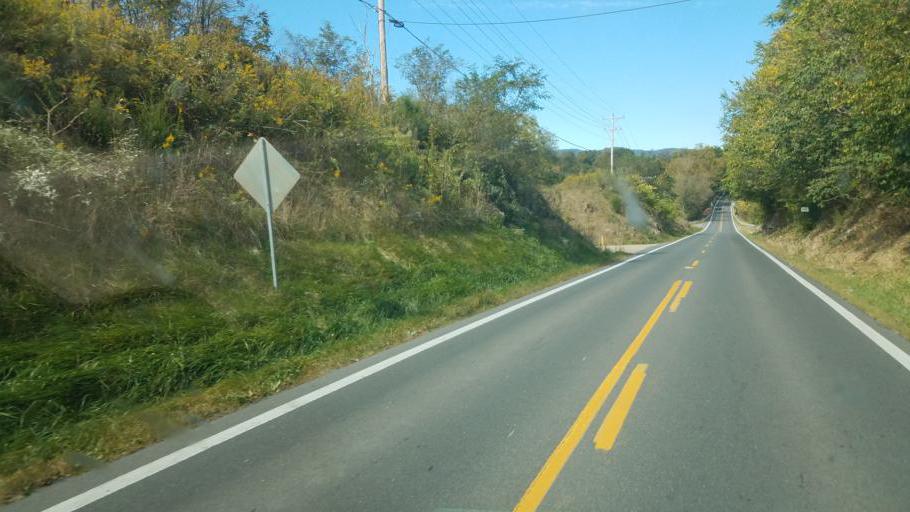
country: US
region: Virginia
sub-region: Page County
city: Luray
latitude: 38.6844
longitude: -78.4549
